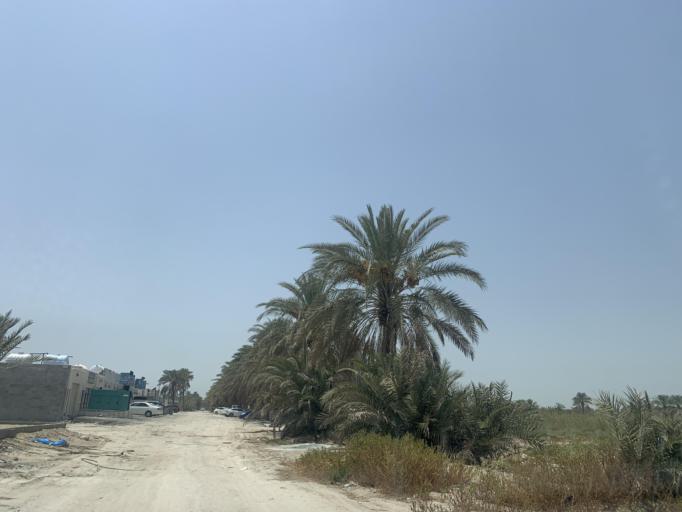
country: BH
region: Central Governorate
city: Madinat Hamad
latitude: 26.1535
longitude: 50.5054
